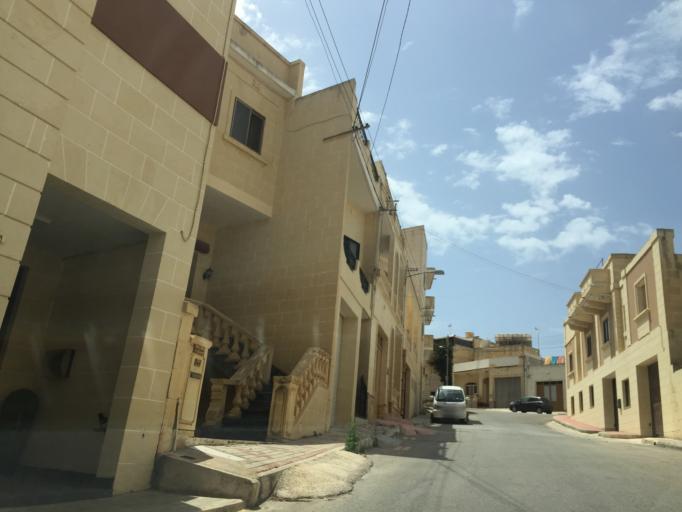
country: MT
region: Ix-Xaghra
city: Xaghra
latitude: 36.0541
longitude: 14.2713
